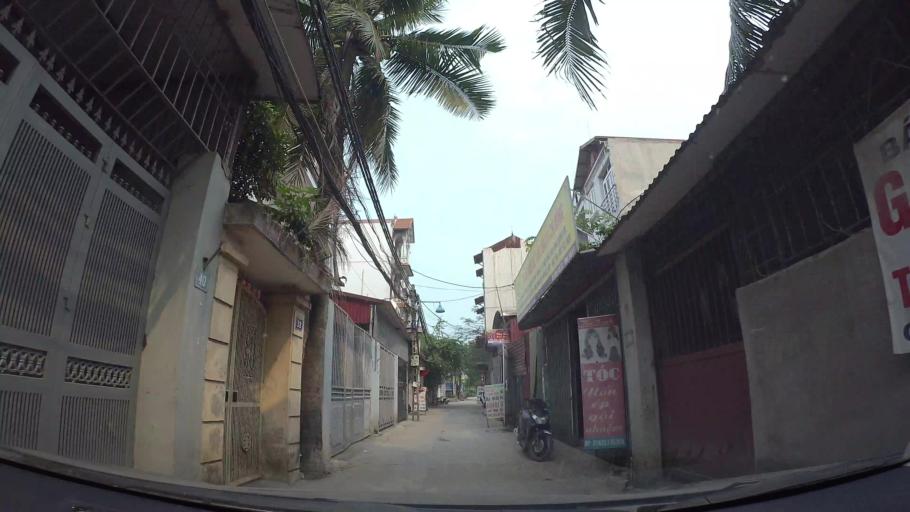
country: VN
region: Ha Noi
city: Trau Quy
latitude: 21.0739
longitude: 105.9036
